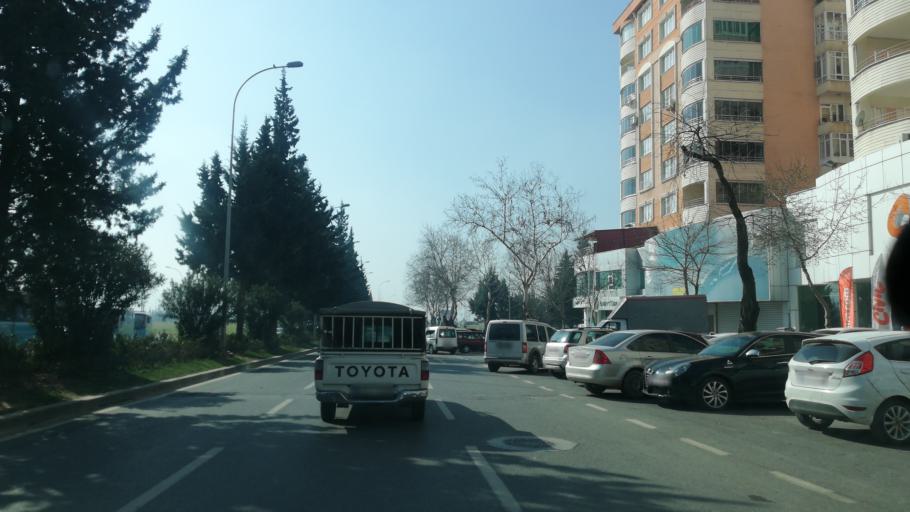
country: TR
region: Kahramanmaras
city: Kahramanmaras
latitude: 37.5705
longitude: 36.9253
